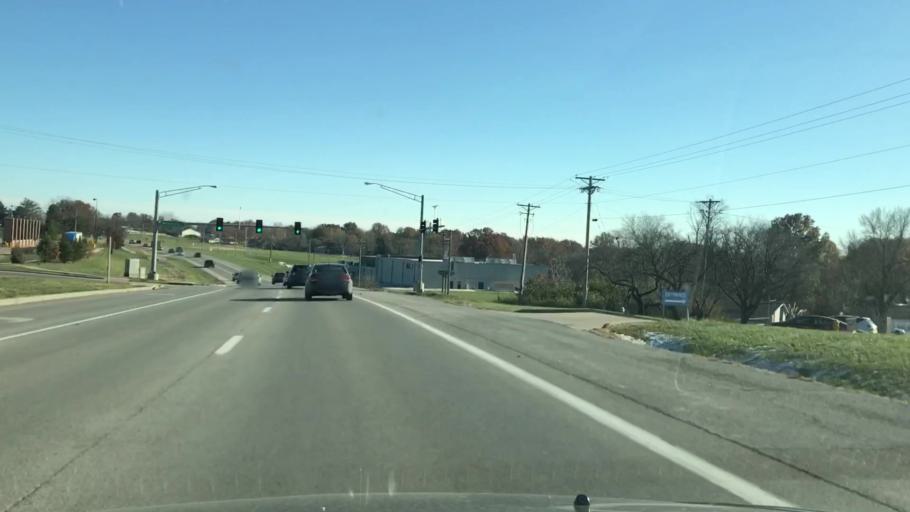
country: US
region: Missouri
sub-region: Jackson County
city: Raytown
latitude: 38.9844
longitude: -94.4627
